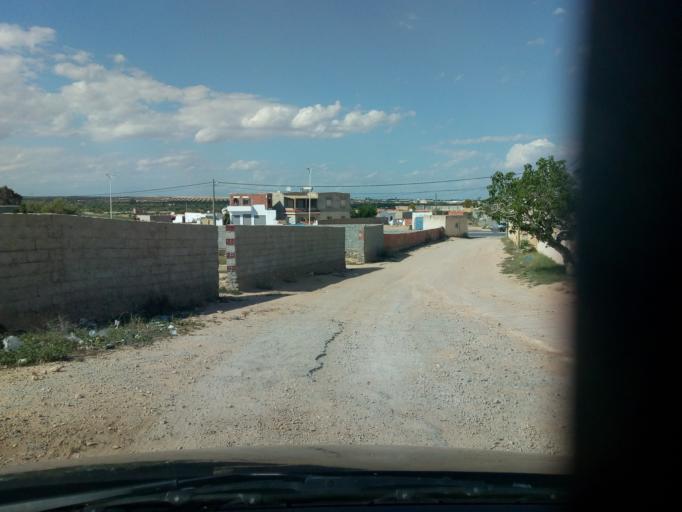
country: TN
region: Safaqis
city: Sfax
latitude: 34.7295
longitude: 10.6055
